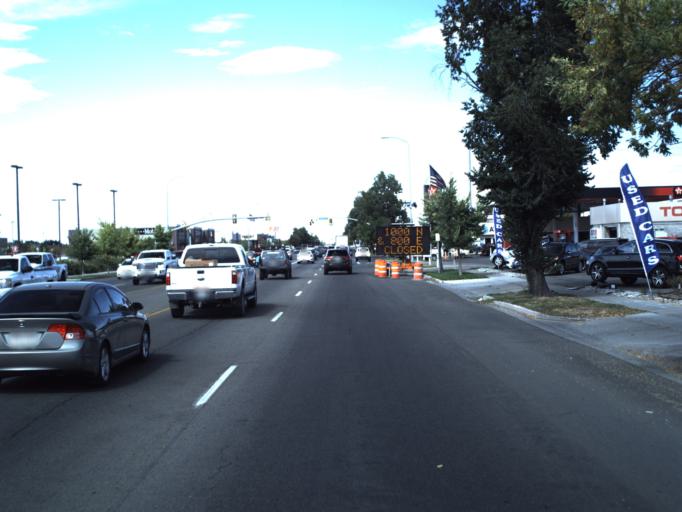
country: US
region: Utah
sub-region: Cache County
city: Logan
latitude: 41.7489
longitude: -111.8344
